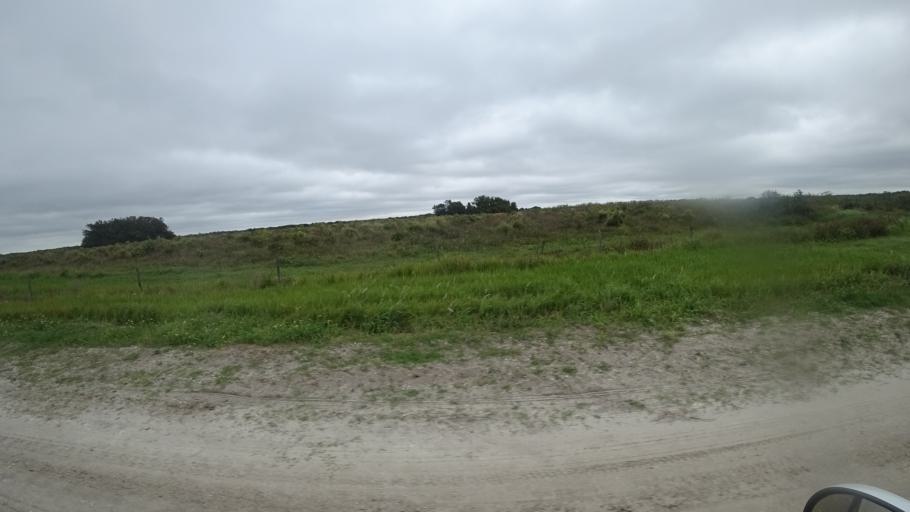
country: US
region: Florida
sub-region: Hillsborough County
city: Wimauma
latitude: 27.5792
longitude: -82.3158
